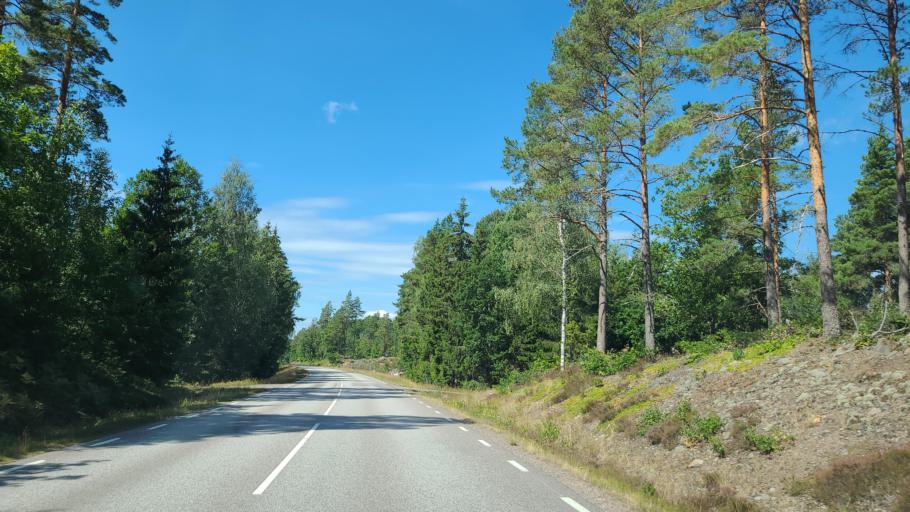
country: SE
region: Kalmar
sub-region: Nybro Kommun
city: Nybro
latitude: 56.5640
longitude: 15.8070
